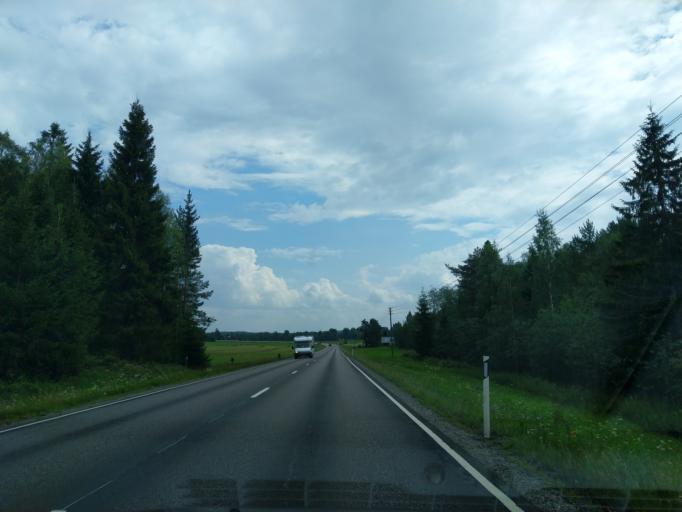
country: FI
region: South Karelia
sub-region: Imatra
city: Parikkala
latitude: 61.6083
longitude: 29.4590
